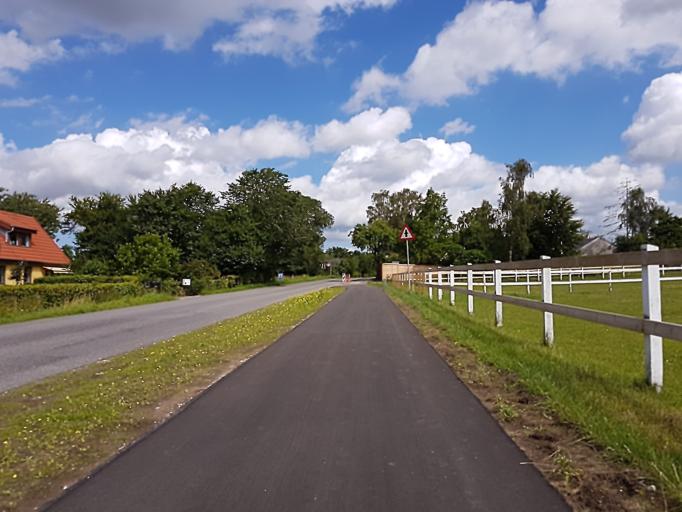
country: DK
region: Capital Region
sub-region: Egedal Kommune
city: Ganlose
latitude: 55.8046
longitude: 12.2829
